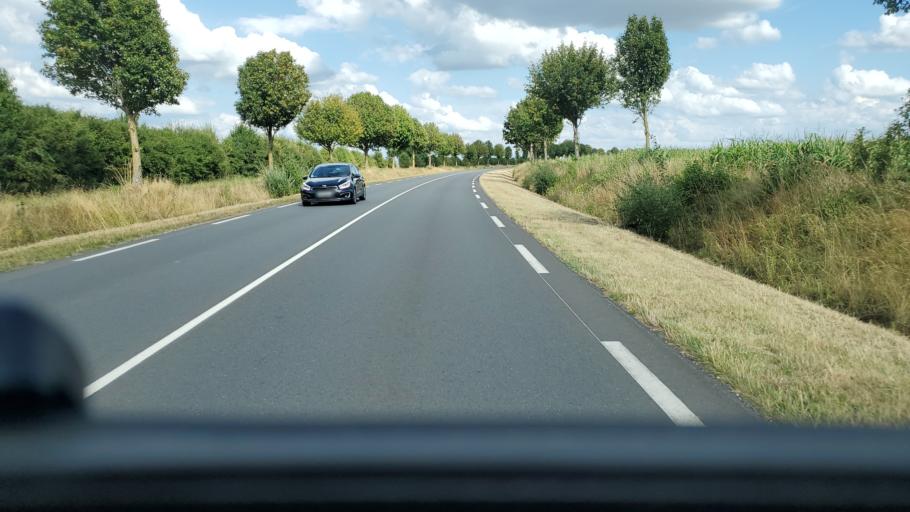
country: FR
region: Ile-de-France
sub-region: Departement de Seine-et-Marne
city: Nanteuil-les-Meaux
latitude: 48.9141
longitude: 2.9085
